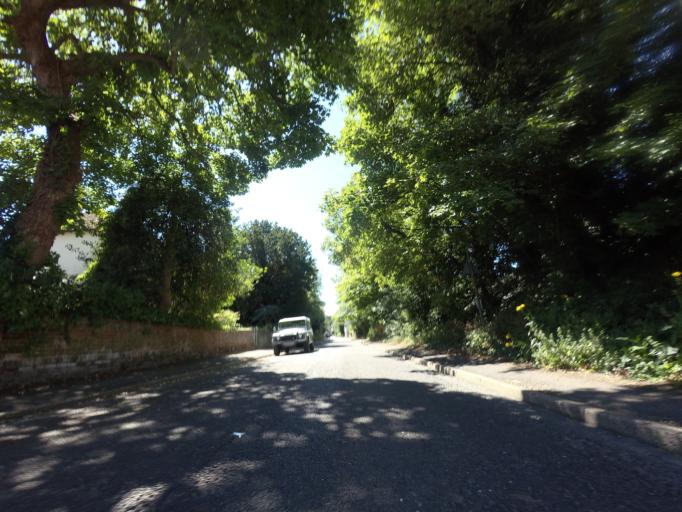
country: GB
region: England
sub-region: Kent
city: Eastry
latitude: 51.2431
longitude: 1.3078
